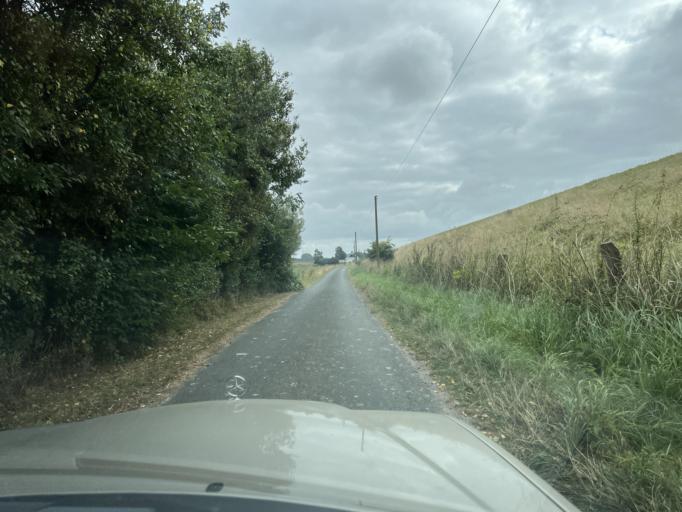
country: DE
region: Schleswig-Holstein
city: Groven
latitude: 54.3215
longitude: 8.9850
